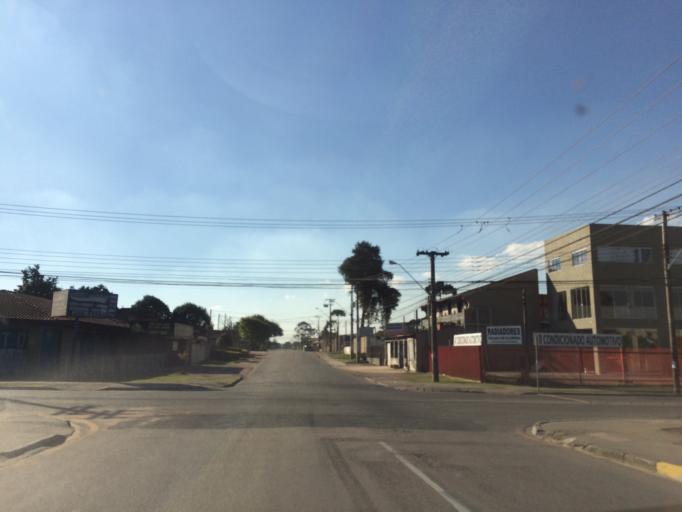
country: BR
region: Parana
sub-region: Sao Jose Dos Pinhais
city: Sao Jose dos Pinhais
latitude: -25.5066
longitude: -49.2337
